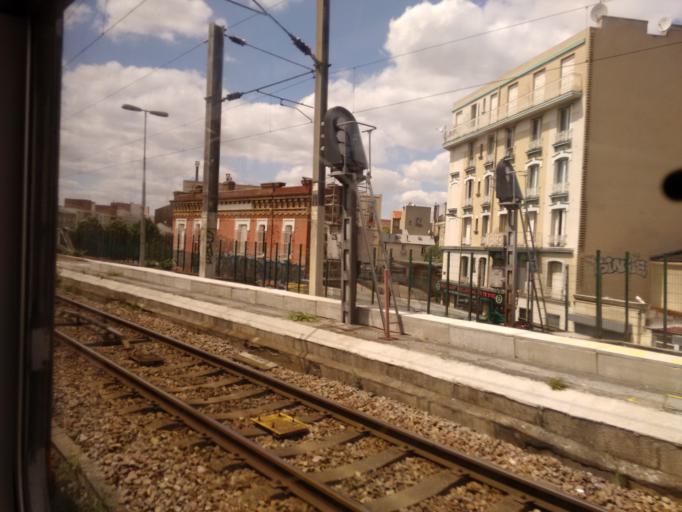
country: FR
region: Ile-de-France
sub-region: Departement de Seine-Saint-Denis
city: Saint-Denis
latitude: 48.9160
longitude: 2.3587
